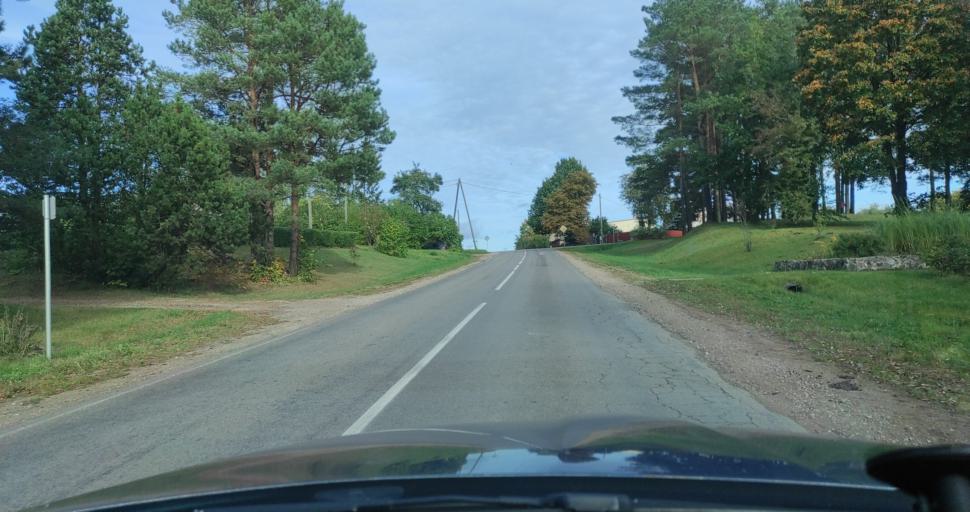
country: LV
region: Jaunpils
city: Jaunpils
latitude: 56.7321
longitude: 23.0133
